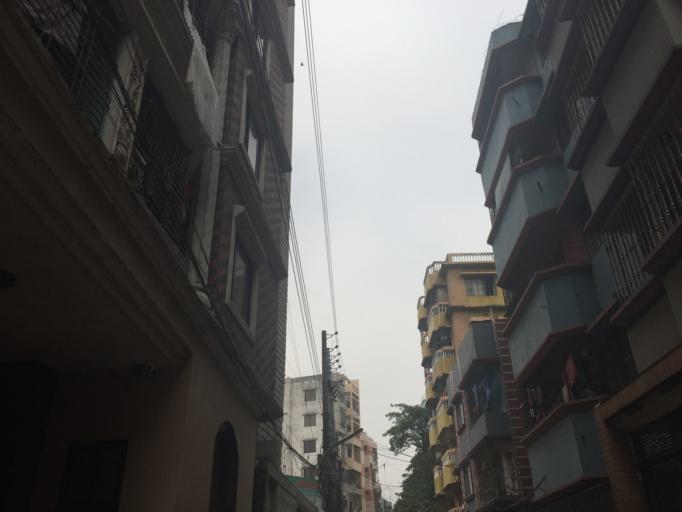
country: BD
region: Dhaka
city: Azimpur
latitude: 23.7799
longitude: 90.3657
